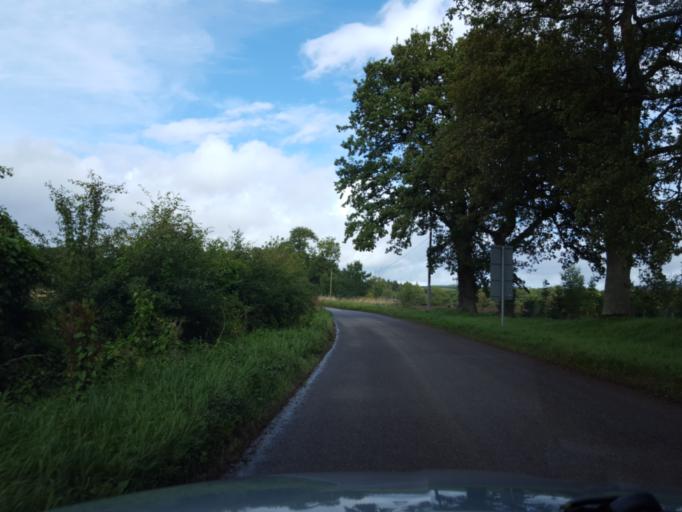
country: GB
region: Scotland
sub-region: Aberdeenshire
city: Laurencekirk
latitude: 56.8549
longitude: -2.5734
